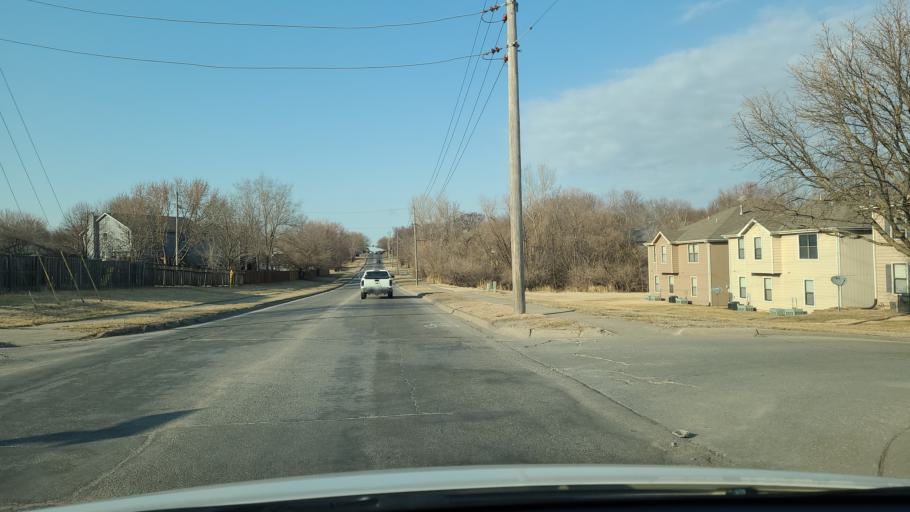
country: US
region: Kansas
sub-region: Douglas County
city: Lawrence
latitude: 38.9666
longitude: -95.2883
